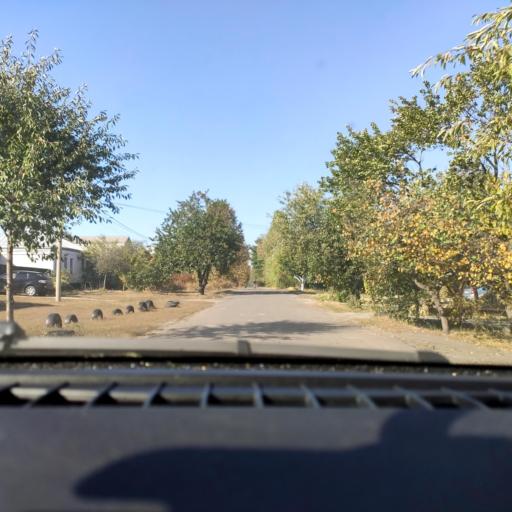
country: RU
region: Voronezj
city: Maslovka
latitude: 51.6151
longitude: 39.2704
